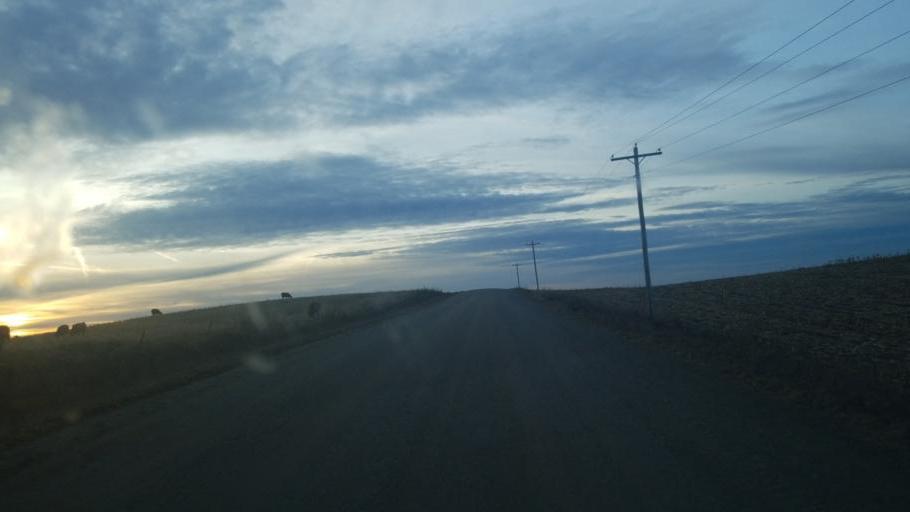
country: US
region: Nebraska
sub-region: Knox County
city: Bloomfield
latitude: 42.6845
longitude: -97.7077
